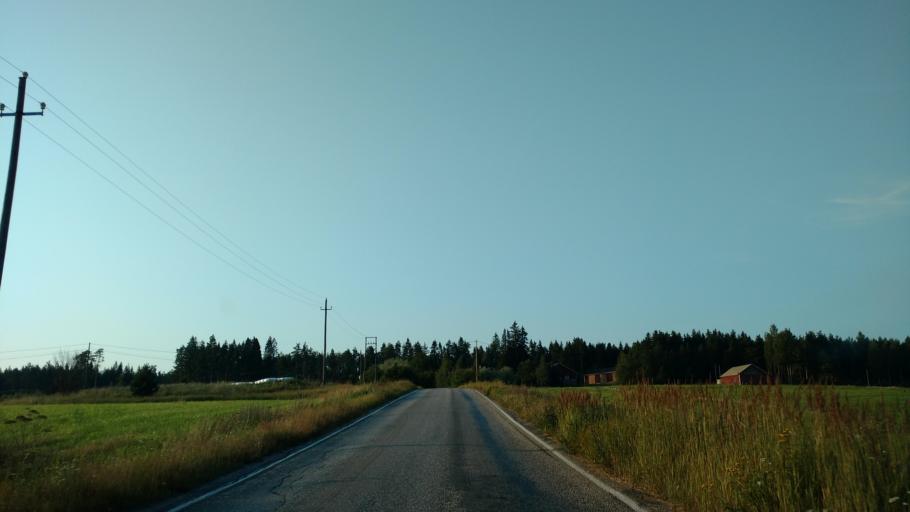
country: FI
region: Varsinais-Suomi
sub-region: Salo
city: Saerkisalo
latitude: 60.1773
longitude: 22.9658
